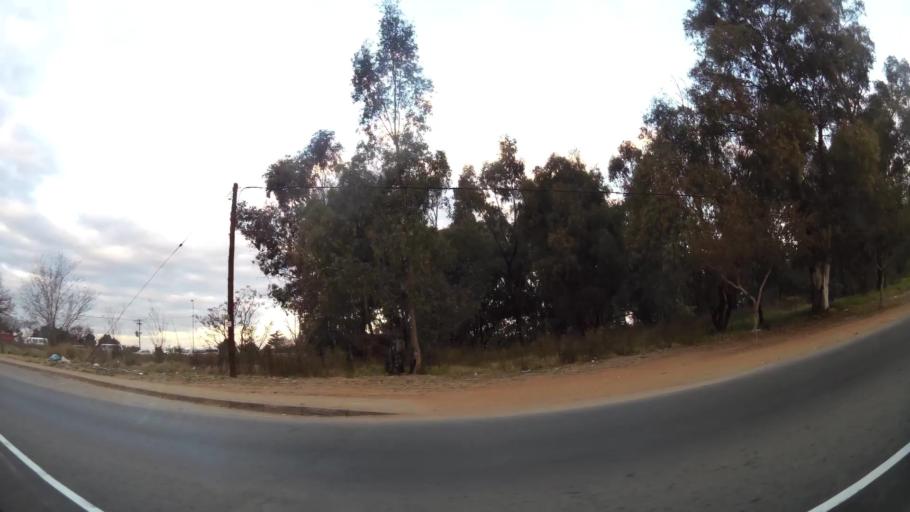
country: ZA
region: Gauteng
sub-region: City of Johannesburg Metropolitan Municipality
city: Midrand
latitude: -25.9897
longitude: 28.1524
